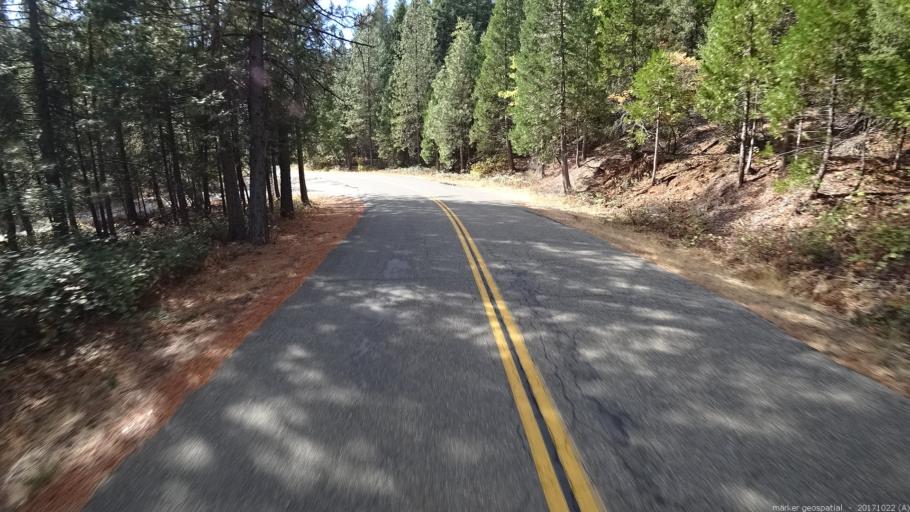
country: US
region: California
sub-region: Siskiyou County
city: Dunsmuir
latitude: 41.0677
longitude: -122.3598
